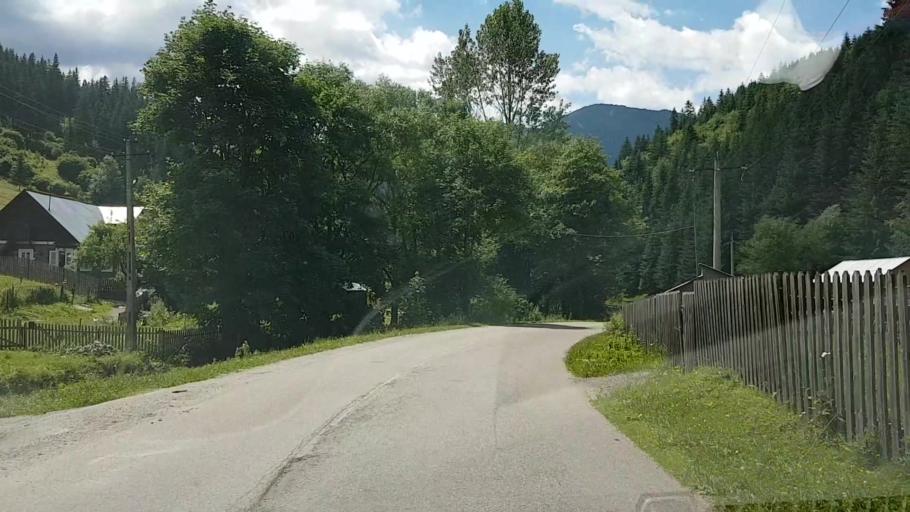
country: RO
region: Suceava
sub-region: Comuna Crucea
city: Crucea
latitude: 47.4131
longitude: 25.5829
